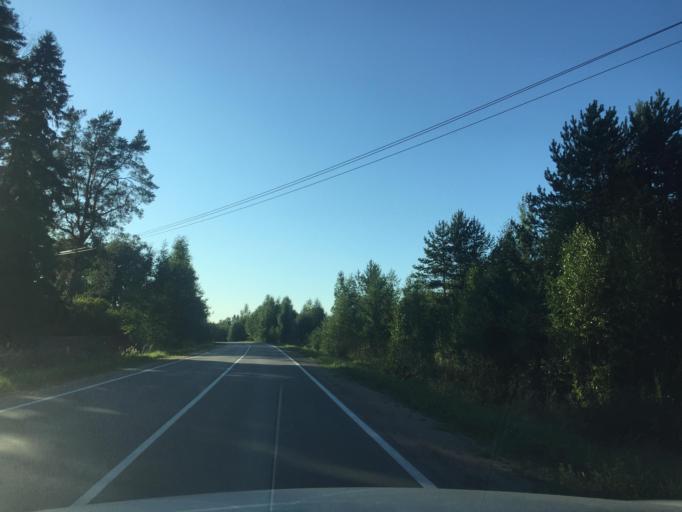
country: RU
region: Leningrad
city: Siverskiy
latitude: 59.3416
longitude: 30.0213
